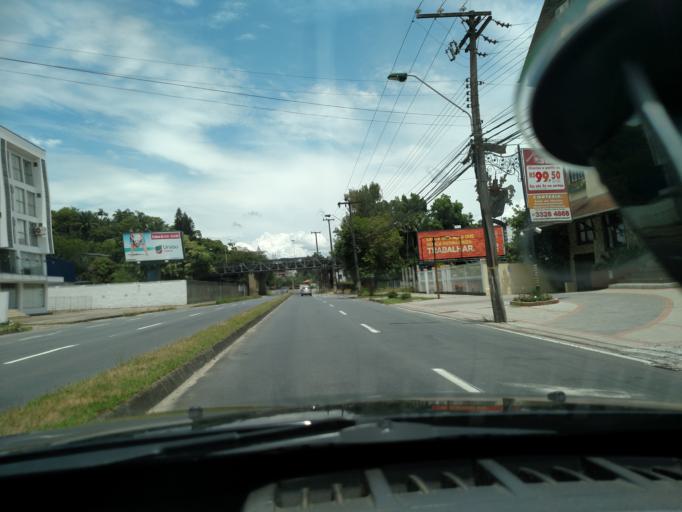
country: BR
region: Santa Catarina
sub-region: Blumenau
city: Blumenau
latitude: -26.9120
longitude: -49.0669
